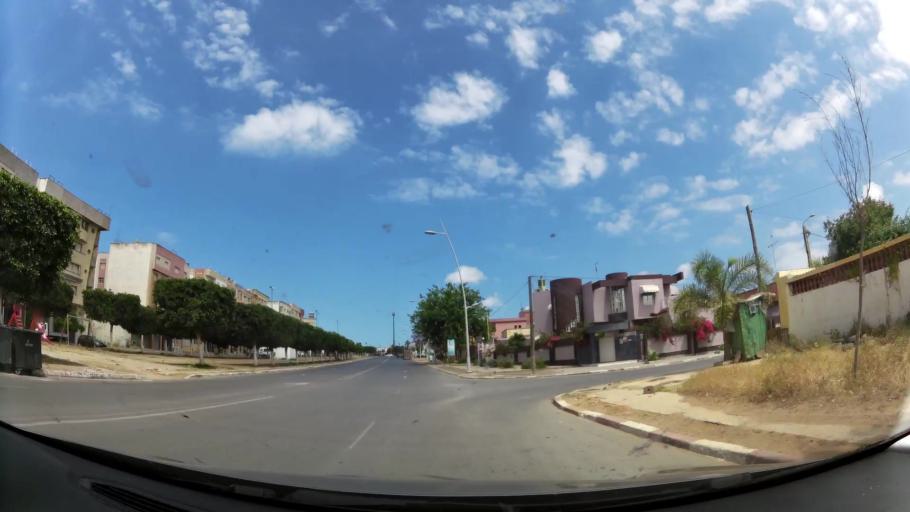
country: MA
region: Gharb-Chrarda-Beni Hssen
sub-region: Kenitra Province
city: Kenitra
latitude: 34.2537
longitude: -6.6021
